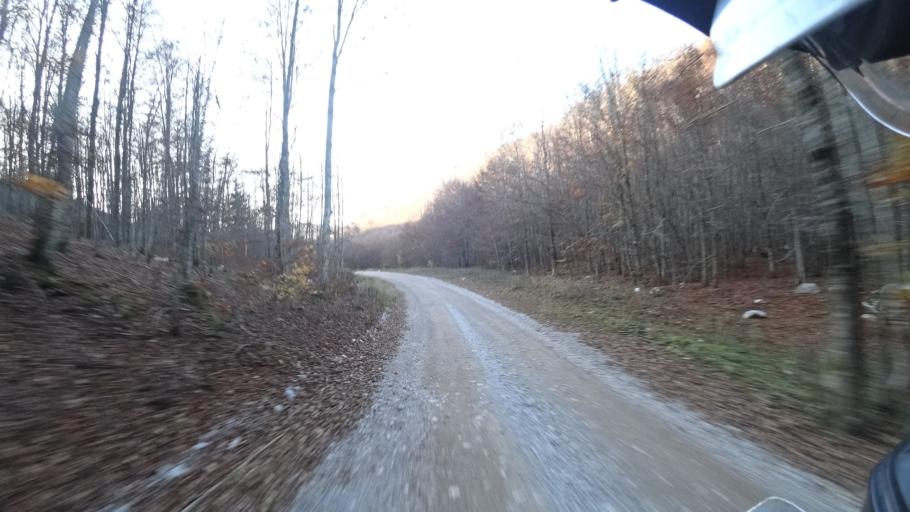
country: HR
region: Primorsko-Goranska
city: Klana
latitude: 45.5008
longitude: 14.4456
